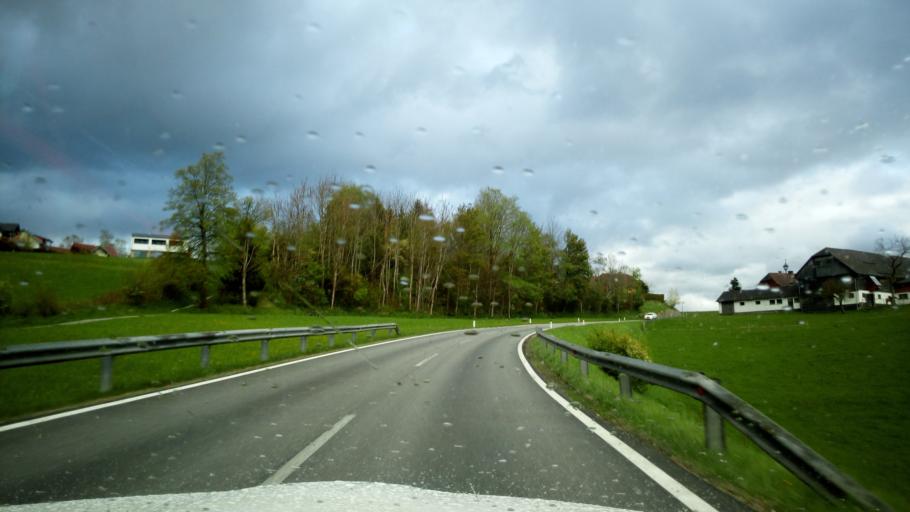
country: AT
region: Styria
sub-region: Politischer Bezirk Liezen
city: Grobming
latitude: 47.4450
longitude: 13.9135
